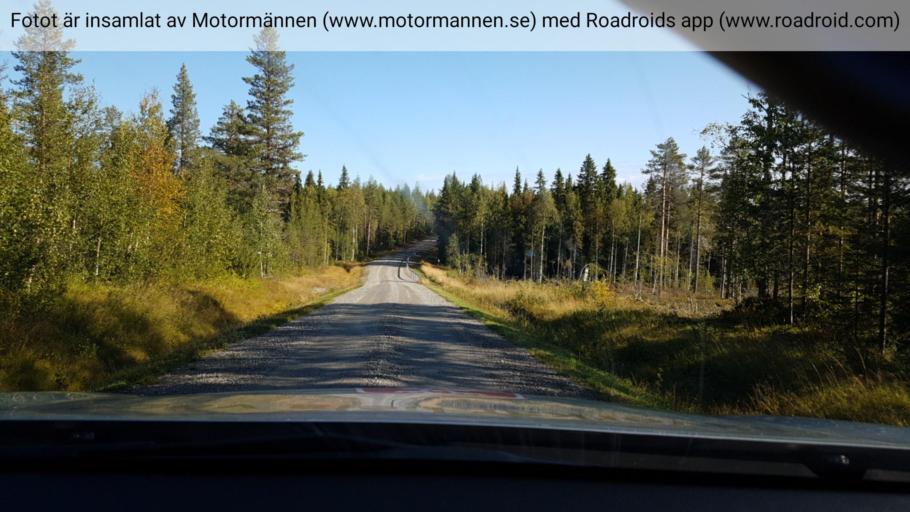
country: SE
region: Vaesterbotten
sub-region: Norsjo Kommun
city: Norsjoe
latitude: 64.6924
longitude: 19.4348
